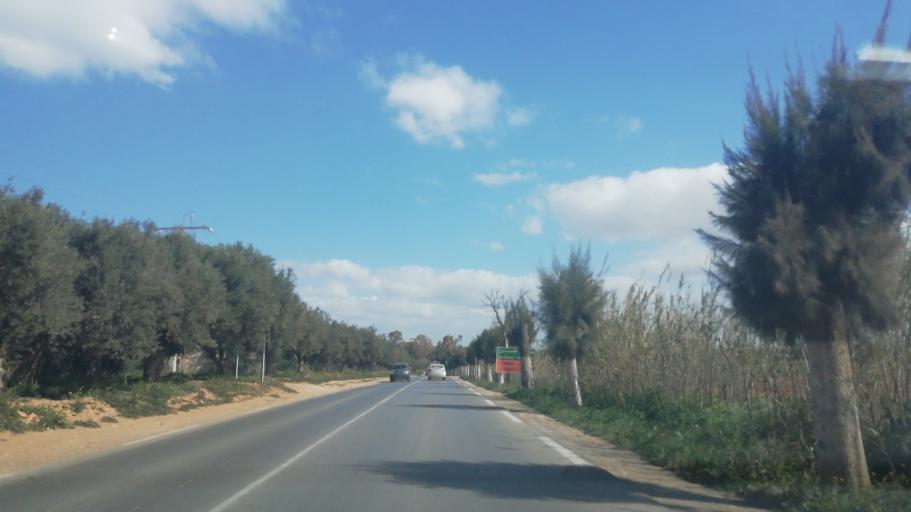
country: DZ
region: Mostaganem
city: Mostaganem
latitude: 35.9992
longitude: 0.3128
